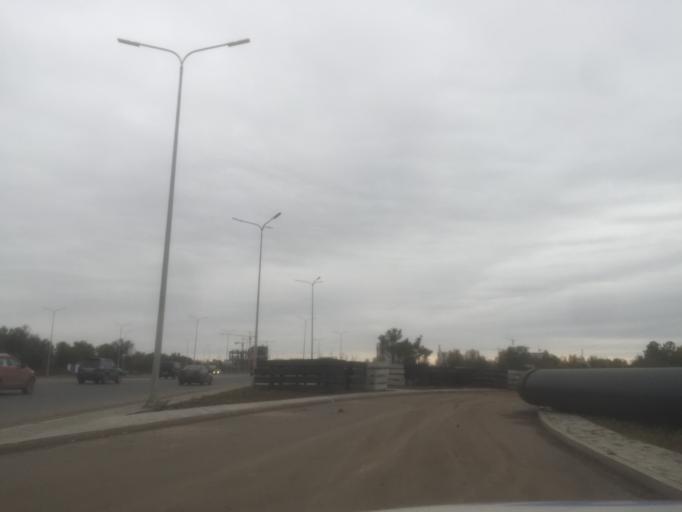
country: KZ
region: Astana Qalasy
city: Astana
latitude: 51.1590
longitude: 71.3725
